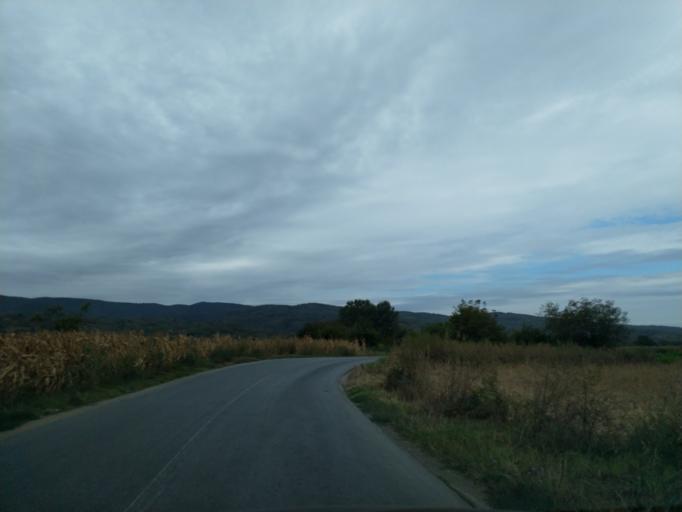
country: RS
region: Central Serbia
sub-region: Pomoravski Okrug
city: Paracin
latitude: 43.8313
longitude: 21.3335
